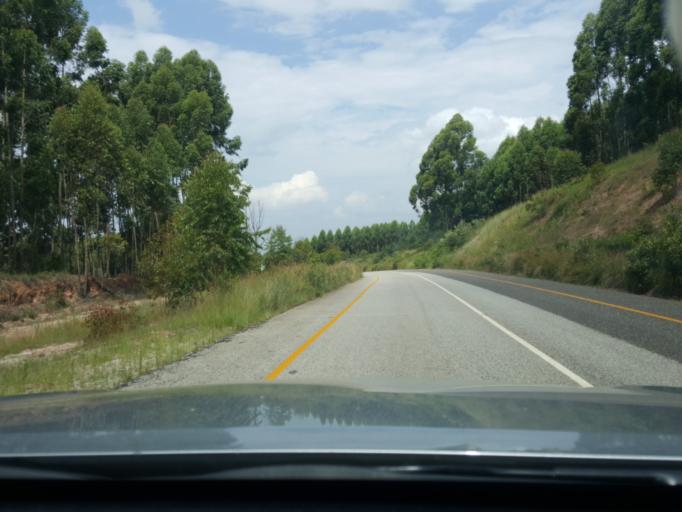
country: ZA
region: Mpumalanga
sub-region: Ehlanzeni District
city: White River
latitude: -25.1862
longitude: 30.8955
